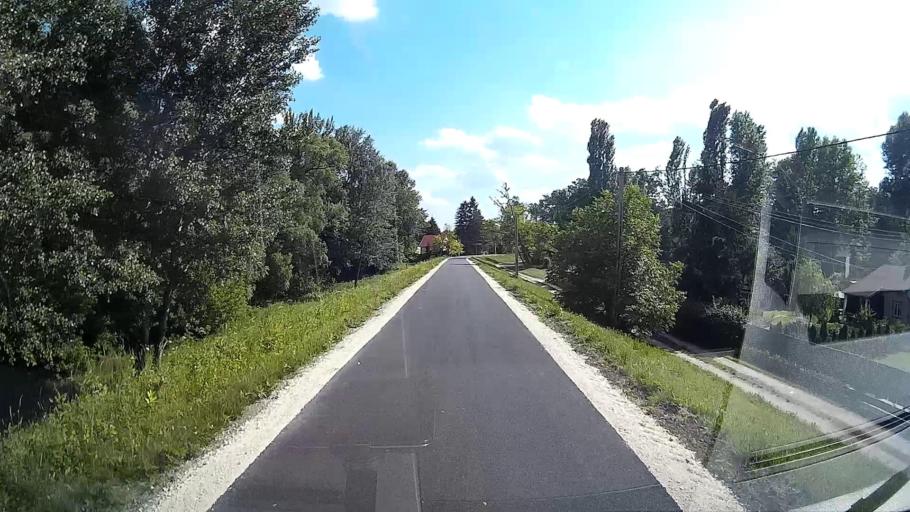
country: HU
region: Pest
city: God
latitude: 47.6678
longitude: 19.1126
